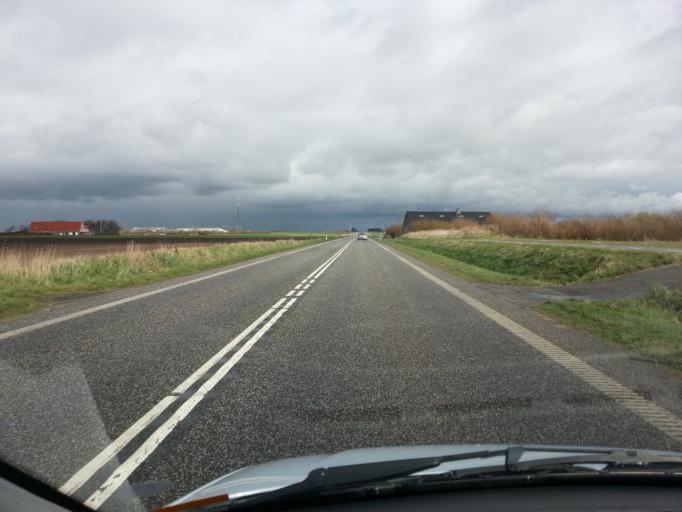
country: DK
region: Central Jutland
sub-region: Ringkobing-Skjern Kommune
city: Ringkobing
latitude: 56.1213
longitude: 8.1411
